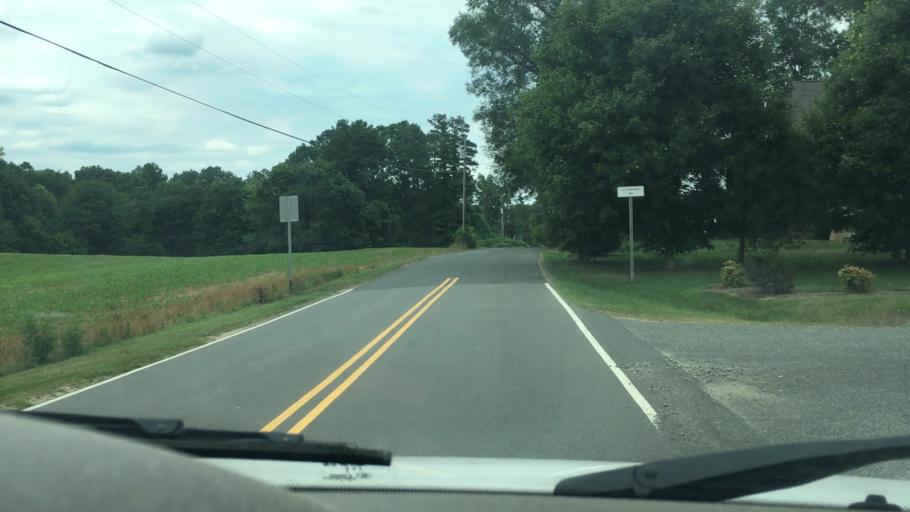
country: US
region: North Carolina
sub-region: Gaston County
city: Davidson
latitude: 35.4599
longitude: -80.7877
